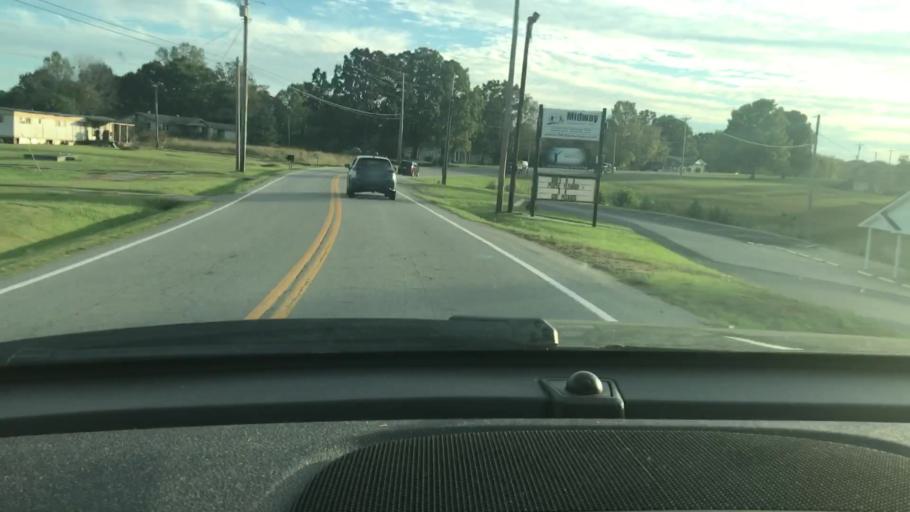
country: US
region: Tennessee
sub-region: Dickson County
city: Charlotte
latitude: 36.2449
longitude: -87.2421
